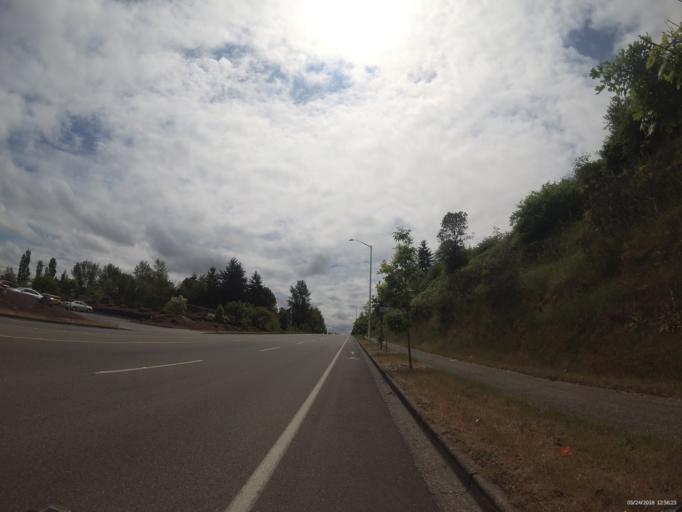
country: US
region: Washington
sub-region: Pierce County
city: Fircrest
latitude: 47.2049
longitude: -122.4931
